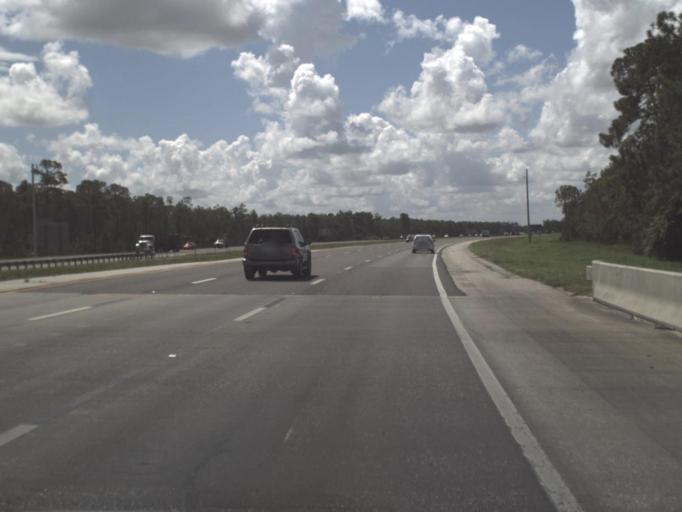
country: US
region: Florida
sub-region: Lee County
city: Estero
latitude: 26.4215
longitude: -81.7742
